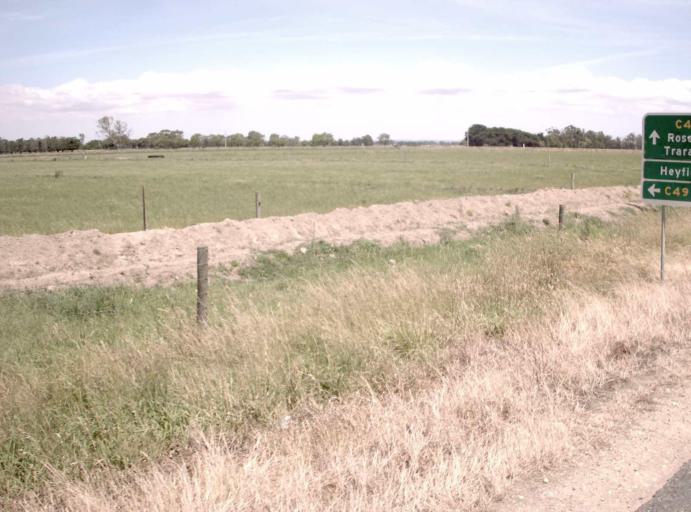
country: AU
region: Victoria
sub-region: Wellington
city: Heyfield
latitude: -38.0227
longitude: 146.8809
